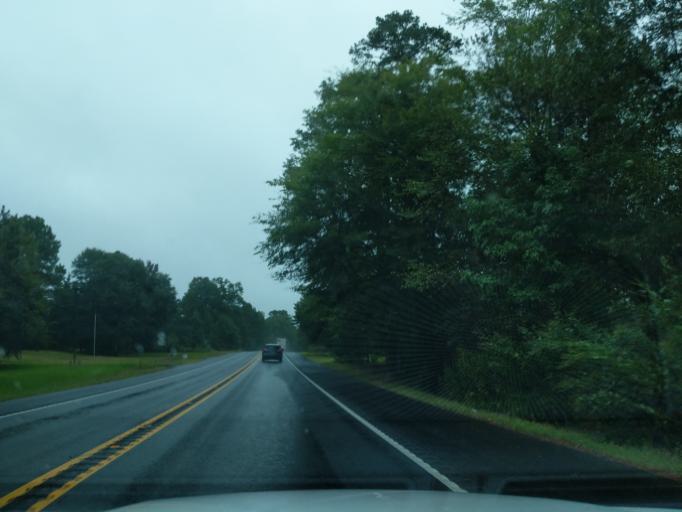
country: US
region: Louisiana
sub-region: Caddo Parish
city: Greenwood
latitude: 32.3796
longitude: -94.0285
